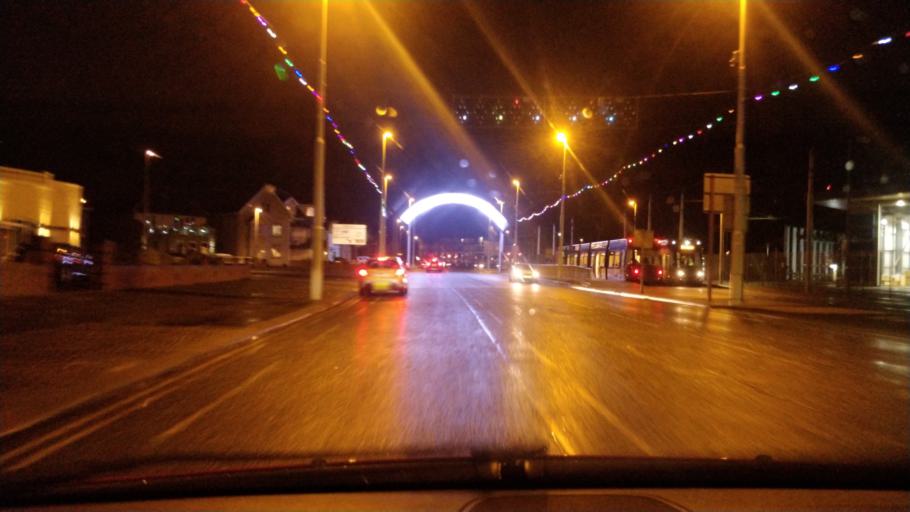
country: GB
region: England
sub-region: Blackpool
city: Blackpool
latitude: 53.7784
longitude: -3.0568
